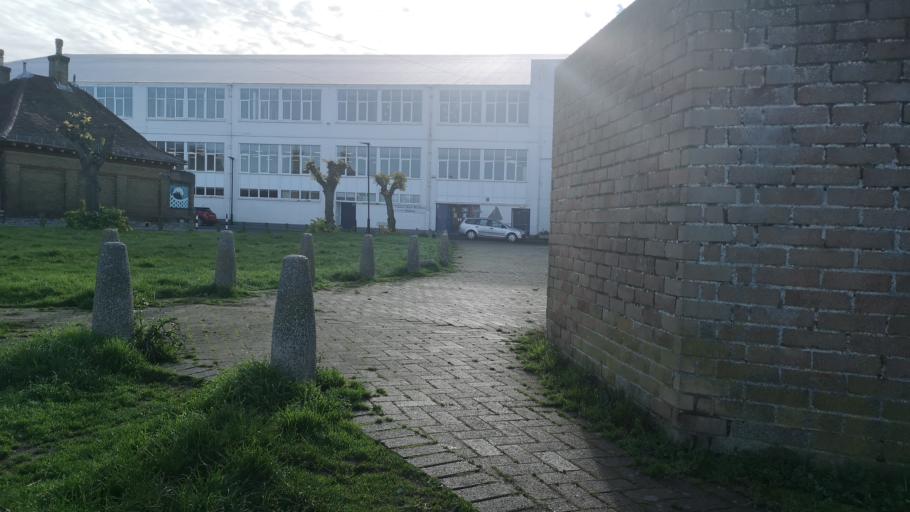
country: GB
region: England
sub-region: Isle of Wight
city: East Cowes
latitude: 50.7609
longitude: -1.2892
